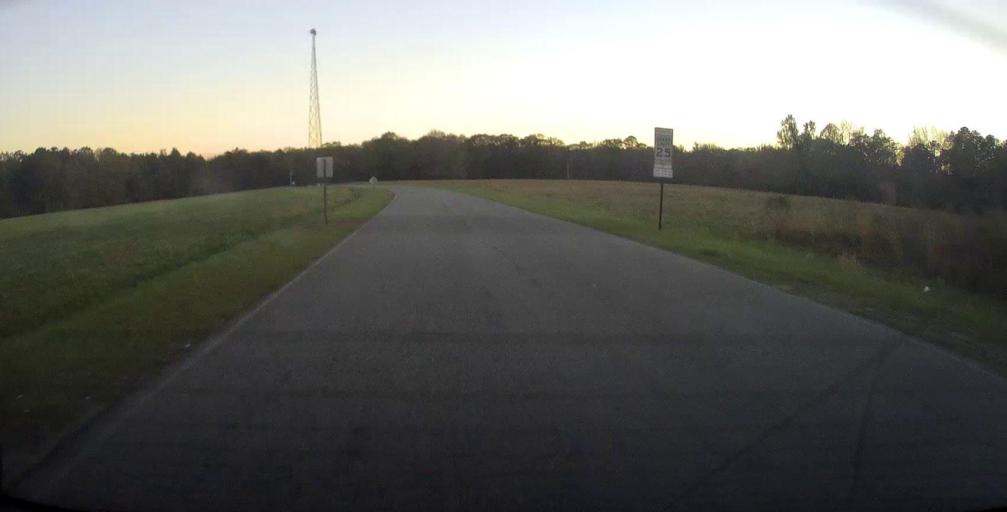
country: US
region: Georgia
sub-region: Crisp County
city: Cordele
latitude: 31.9542
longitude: -83.7534
